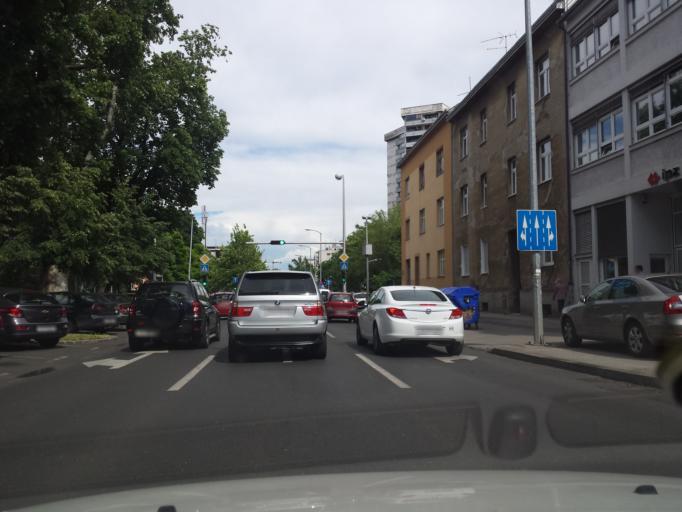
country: HR
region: Grad Zagreb
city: Zagreb - Centar
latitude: 45.8118
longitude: 15.9413
